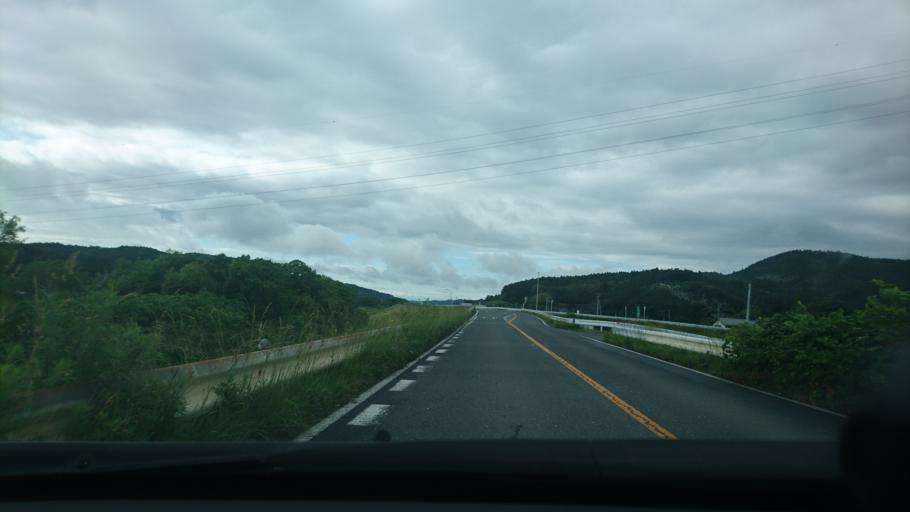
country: JP
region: Miyagi
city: Wakuya
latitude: 38.6175
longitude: 141.2986
